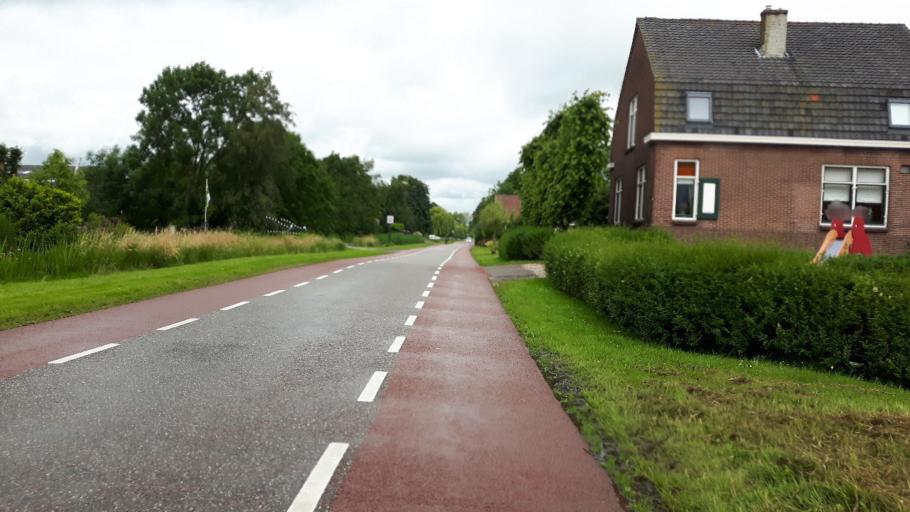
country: NL
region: Utrecht
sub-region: Stichtse Vecht
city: Breukelen
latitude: 52.1663
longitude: 4.9520
